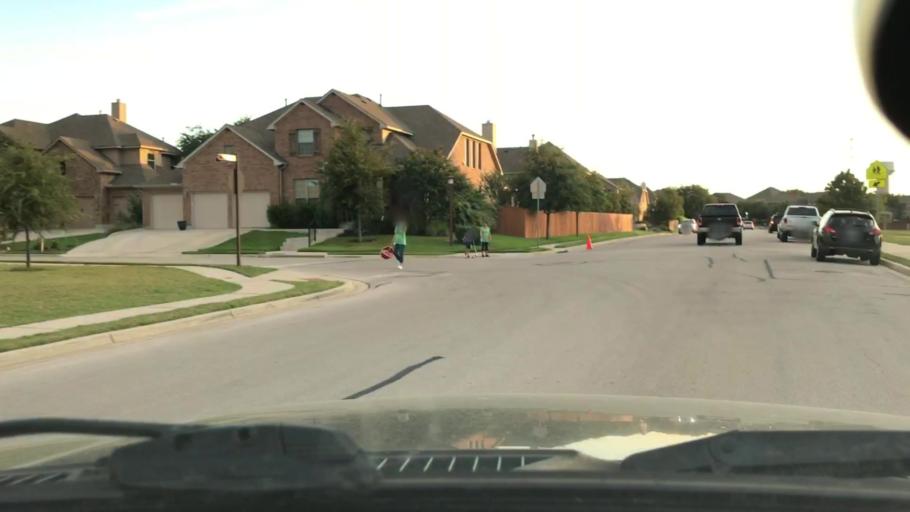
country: US
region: Texas
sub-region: Williamson County
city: Leander
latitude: 30.5378
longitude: -97.8670
